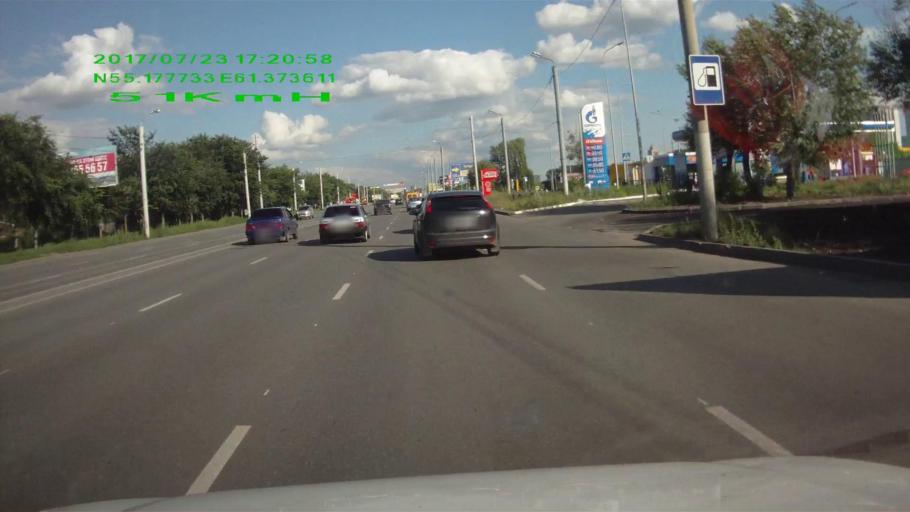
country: RU
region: Chelyabinsk
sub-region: Gorod Chelyabinsk
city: Chelyabinsk
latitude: 55.1775
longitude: 61.3743
